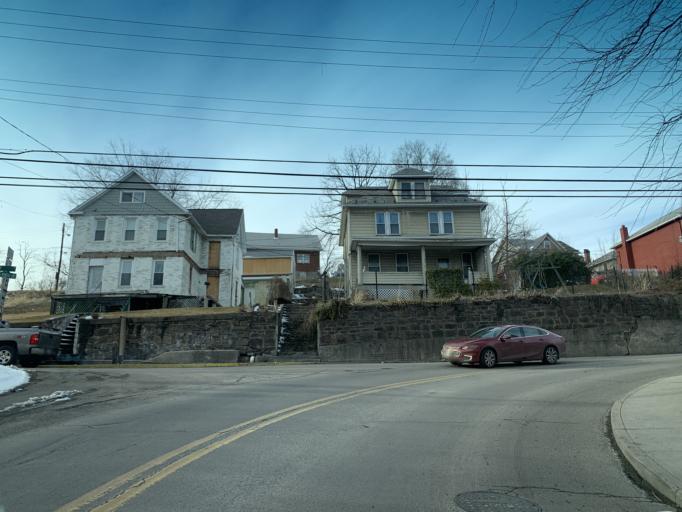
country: US
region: Maryland
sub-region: Allegany County
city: Cumberland
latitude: 39.6468
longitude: -78.7667
